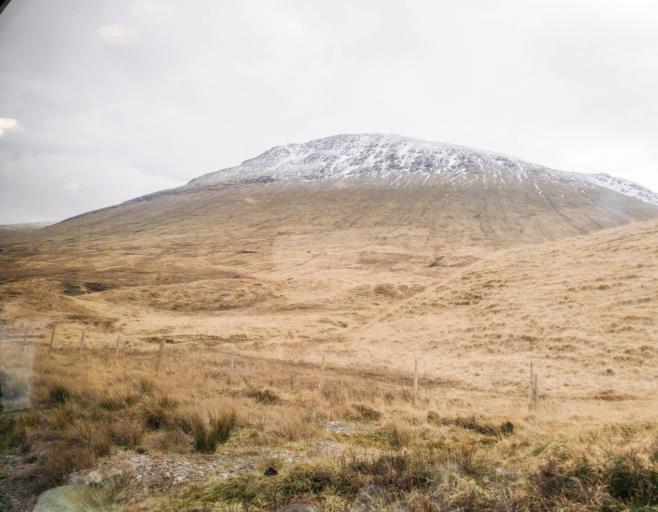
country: GB
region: Scotland
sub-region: Highland
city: Spean Bridge
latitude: 56.5560
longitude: -4.7273
